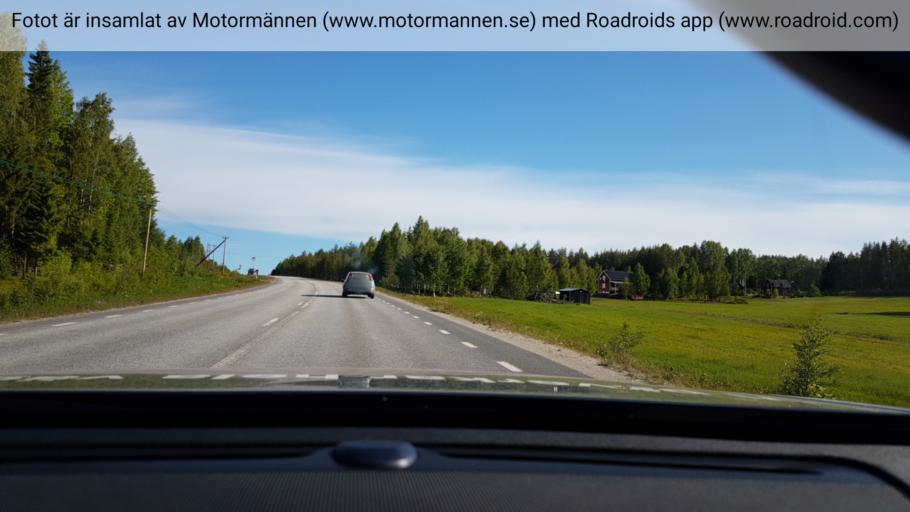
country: SE
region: Vaesterbotten
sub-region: Vannas Kommun
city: Vaennaes
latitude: 64.0266
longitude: 19.6926
